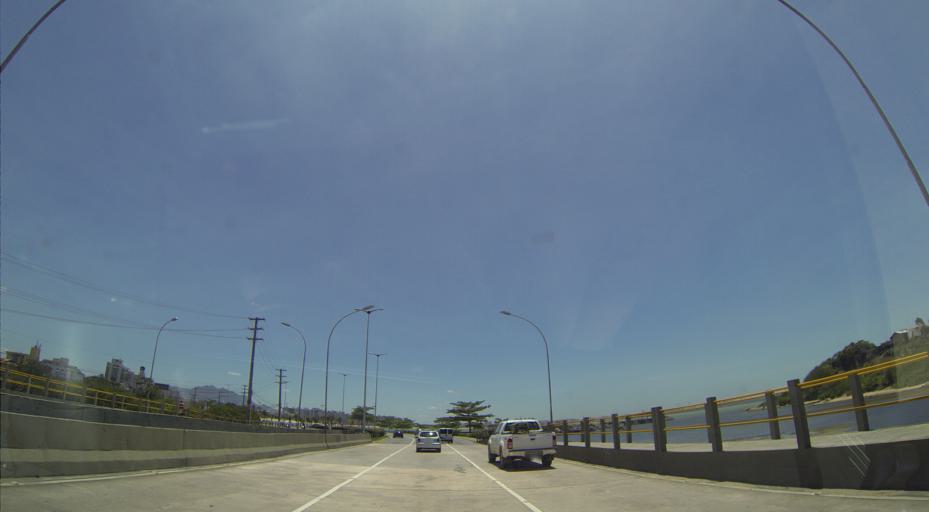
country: BR
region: Espirito Santo
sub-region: Vila Velha
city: Vila Velha
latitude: -20.2948
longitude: -40.2894
